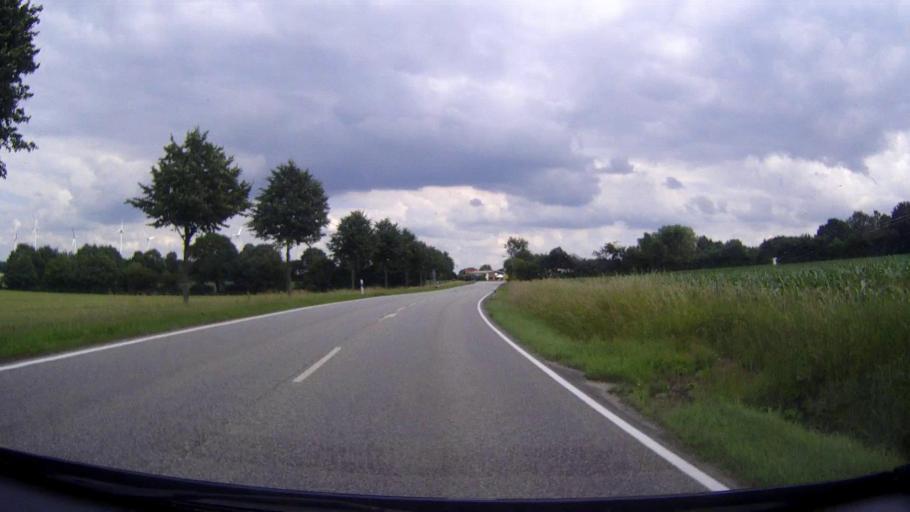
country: DE
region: Schleswig-Holstein
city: Gokels
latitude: 54.1162
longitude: 9.4618
